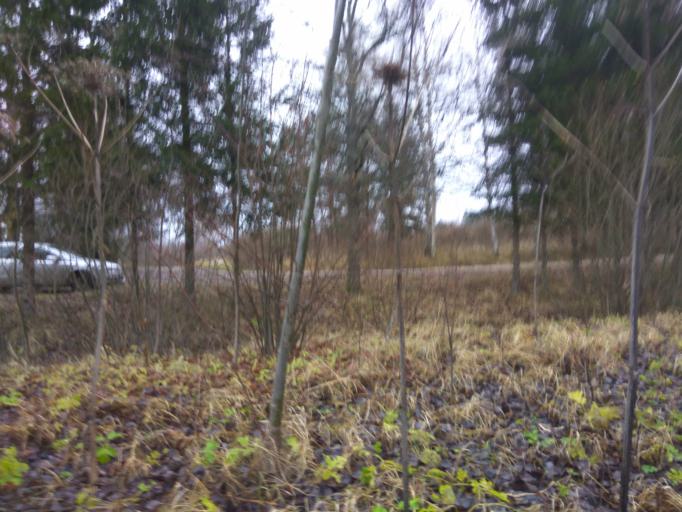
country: LV
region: Kuldigas Rajons
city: Kuldiga
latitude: 56.9322
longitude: 22.0081
